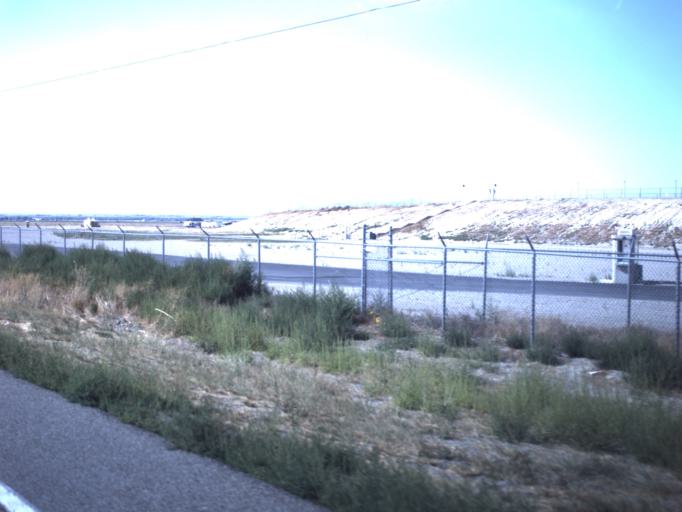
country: US
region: Utah
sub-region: Tooele County
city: Grantsville
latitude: 40.5753
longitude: -112.3863
